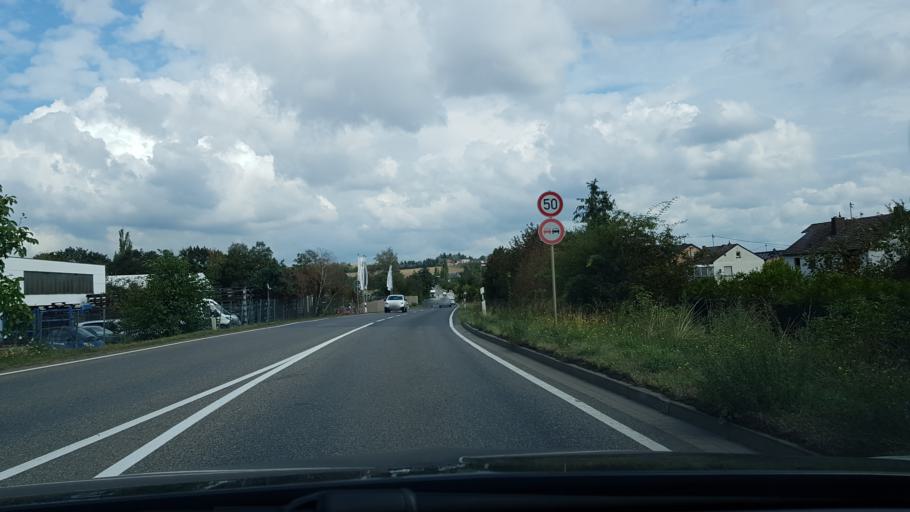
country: DE
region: Rheinland-Pfalz
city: Plaidt
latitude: 50.3909
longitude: 7.3820
